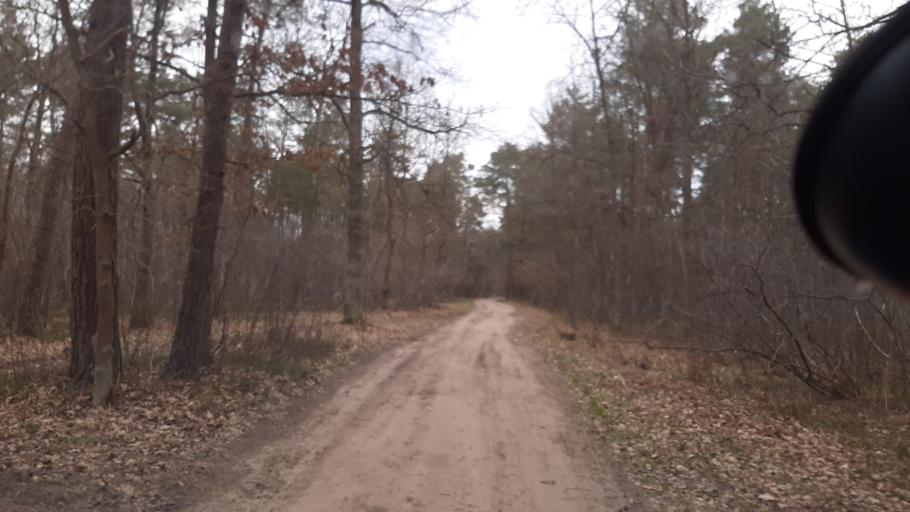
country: PL
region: Lublin Voivodeship
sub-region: Powiat lubartowski
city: Abramow
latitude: 51.4394
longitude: 22.3452
